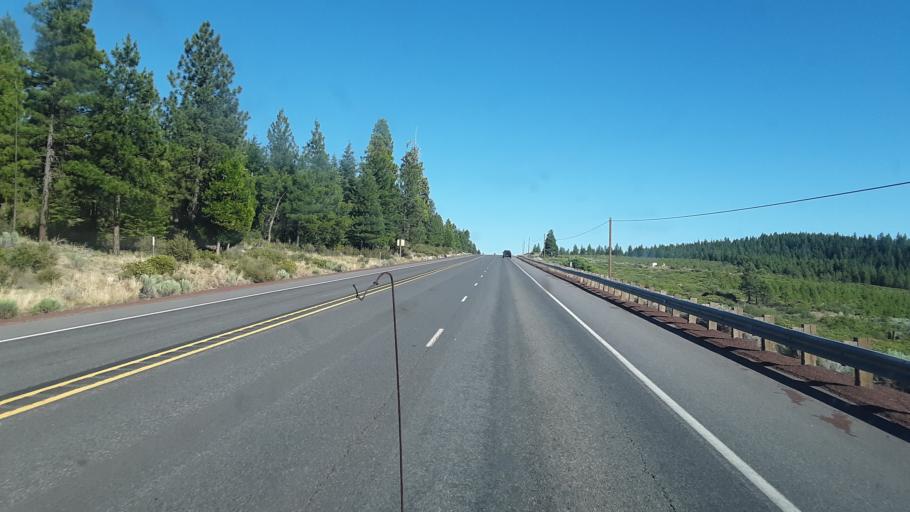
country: US
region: Oregon
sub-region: Klamath County
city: Klamath Falls
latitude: 42.3566
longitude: -121.9881
